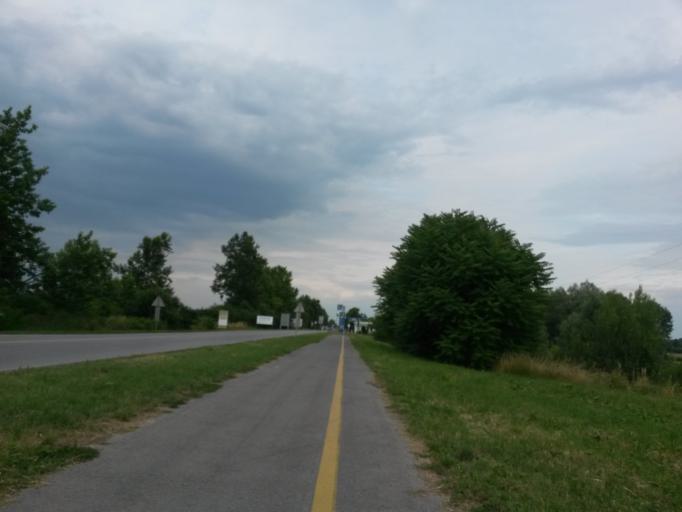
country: HR
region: Osjecko-Baranjska
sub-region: Grad Osijek
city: Osijek
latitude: 45.5690
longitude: 18.7087
